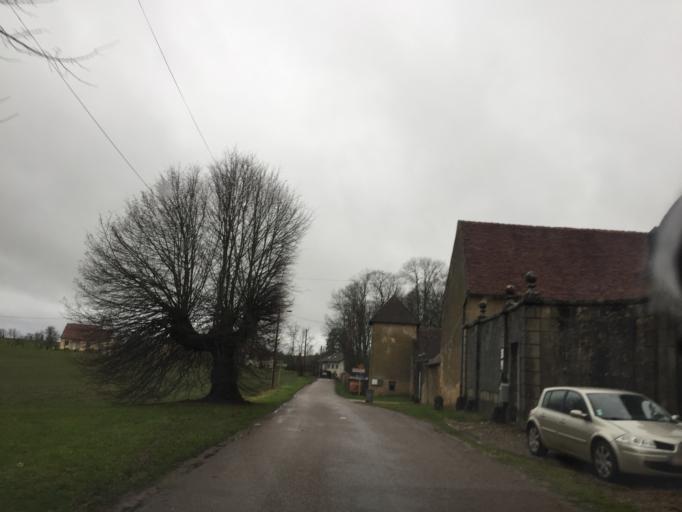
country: FR
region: Franche-Comte
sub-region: Departement du Jura
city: Orchamps
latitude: 47.1958
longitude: 5.6538
